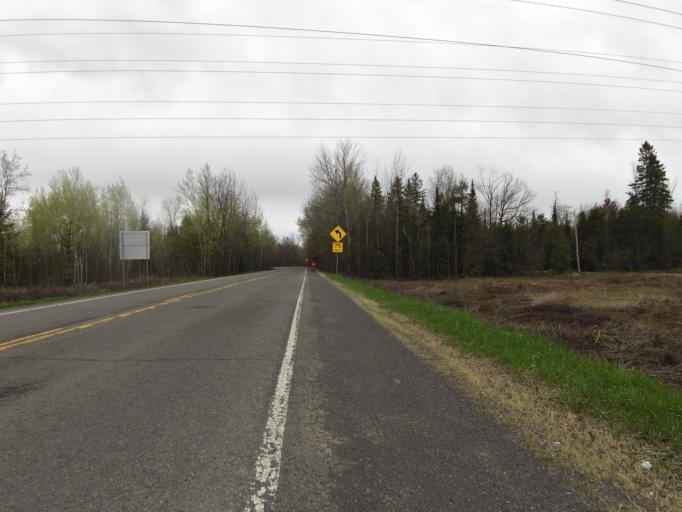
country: CA
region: Quebec
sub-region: Laurentides
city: Lachute
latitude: 45.5734
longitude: -74.3744
